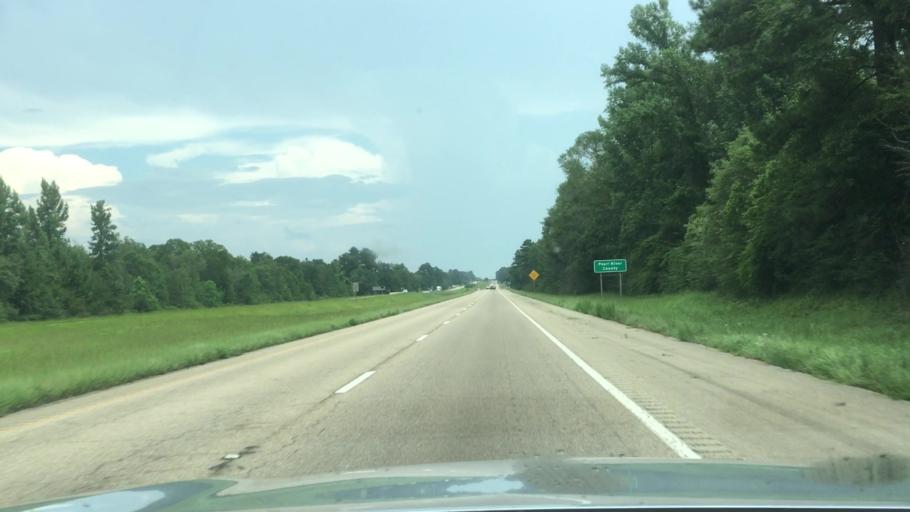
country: US
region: Mississippi
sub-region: Lamar County
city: Lumberton
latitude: 30.9877
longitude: -89.4252
